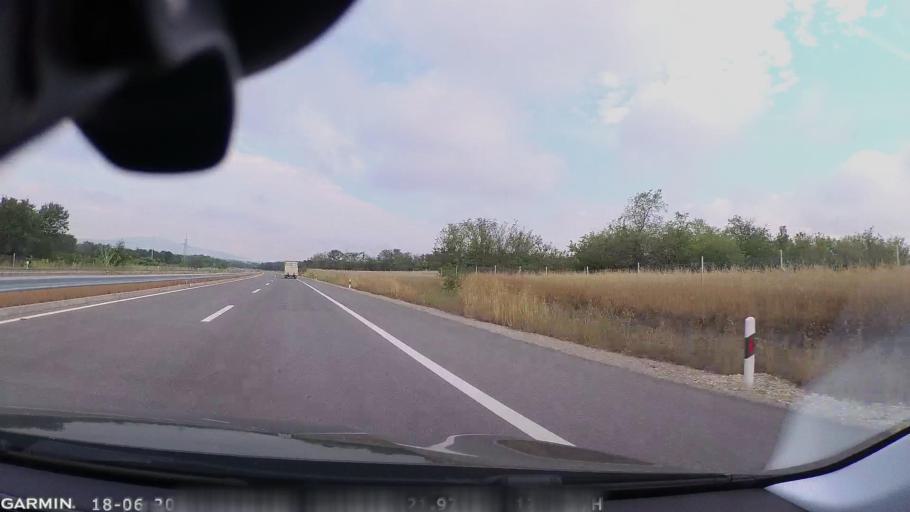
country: MK
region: Sveti Nikole
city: Sveti Nikole
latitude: 41.8435
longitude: 21.9779
